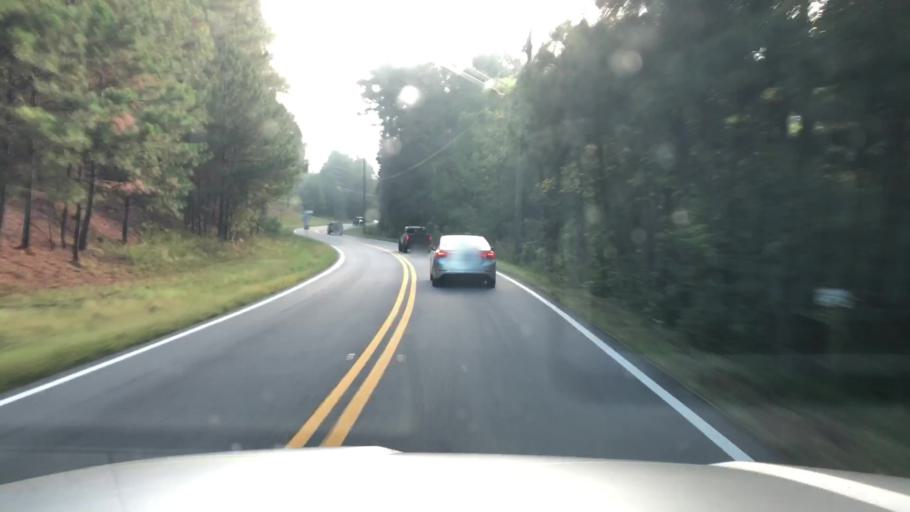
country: US
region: Georgia
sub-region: Bartow County
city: Emerson
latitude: 34.0781
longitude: -84.7700
